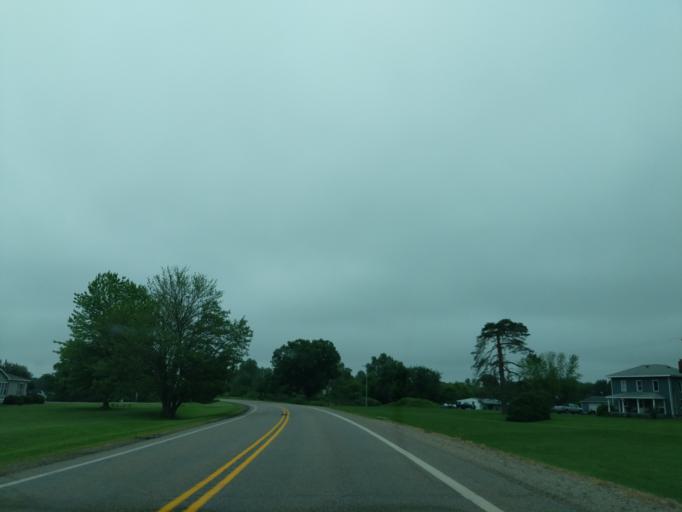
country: US
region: Michigan
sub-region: Hillsdale County
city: Litchfield
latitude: 42.0755
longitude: -84.8016
